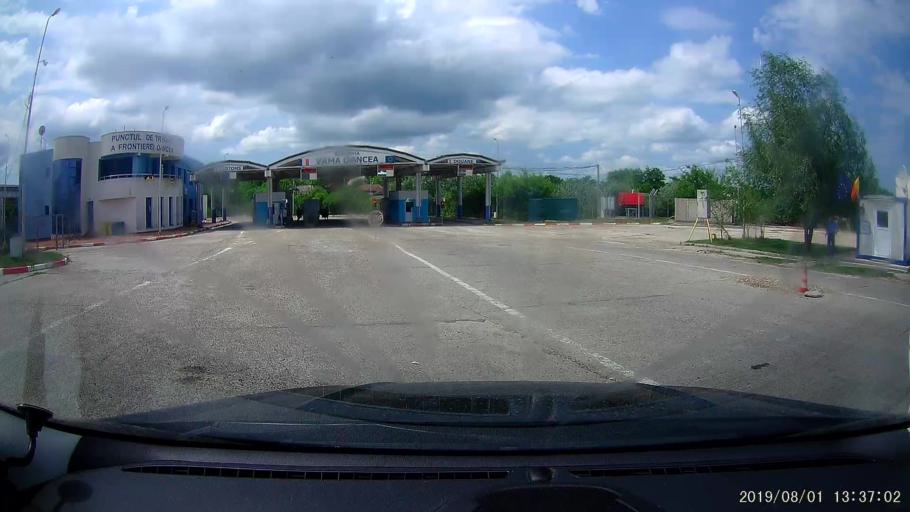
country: RO
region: Galati
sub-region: Comuna Oancea
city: Oancea
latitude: 45.9178
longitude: 28.1186
